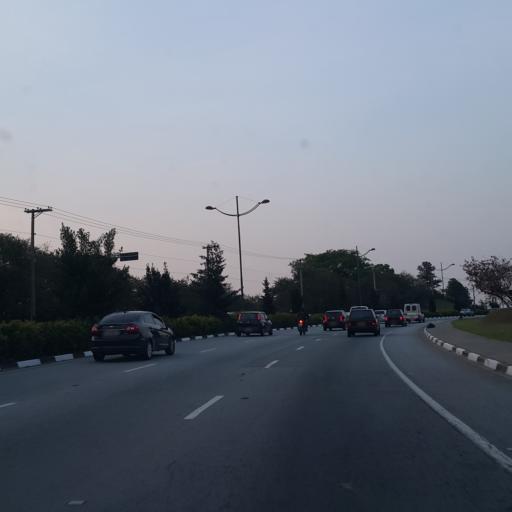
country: BR
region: Sao Paulo
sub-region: Vinhedo
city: Vinhedo
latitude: -23.0453
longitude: -46.9849
